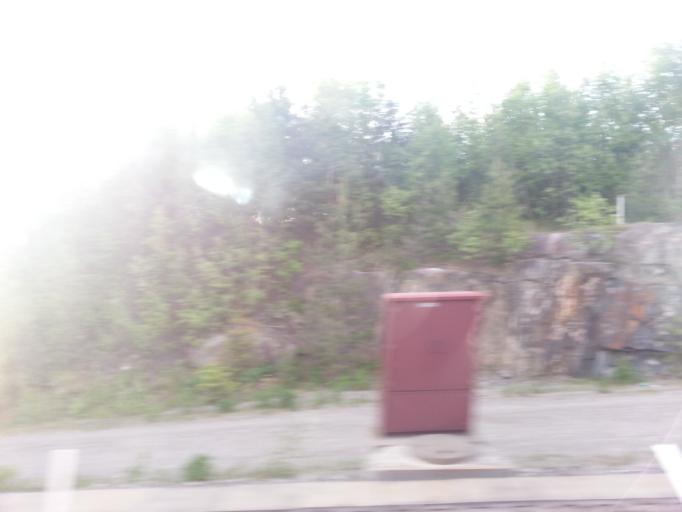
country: NO
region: Akershus
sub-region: Nannestad
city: Teigebyen
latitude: 60.2066
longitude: 11.1046
